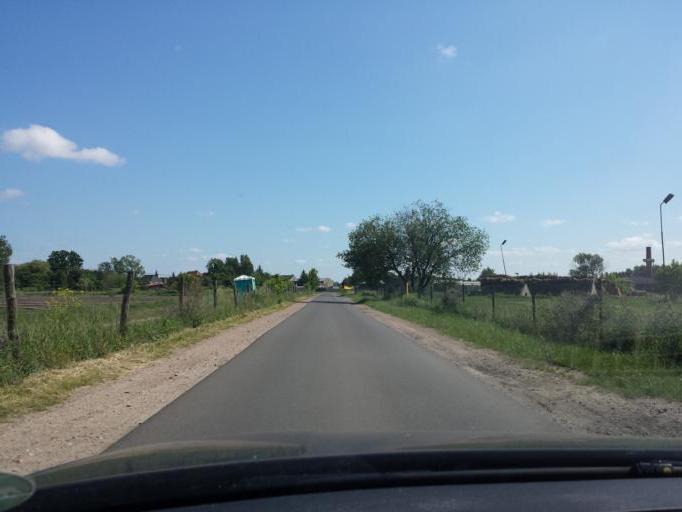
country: DE
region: Brandenburg
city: Kremmen
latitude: 52.8166
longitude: 13.0014
